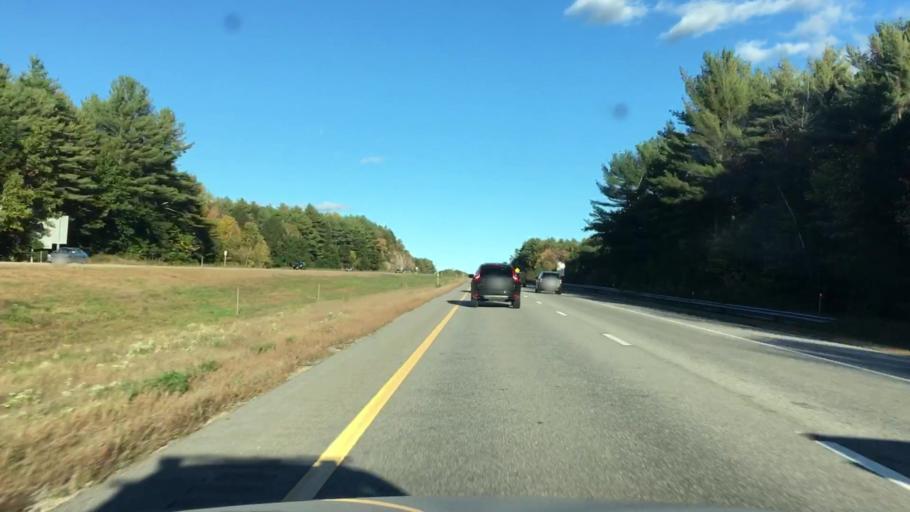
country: US
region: New Hampshire
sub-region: Rockingham County
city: Candia
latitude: 43.0386
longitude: -71.3030
